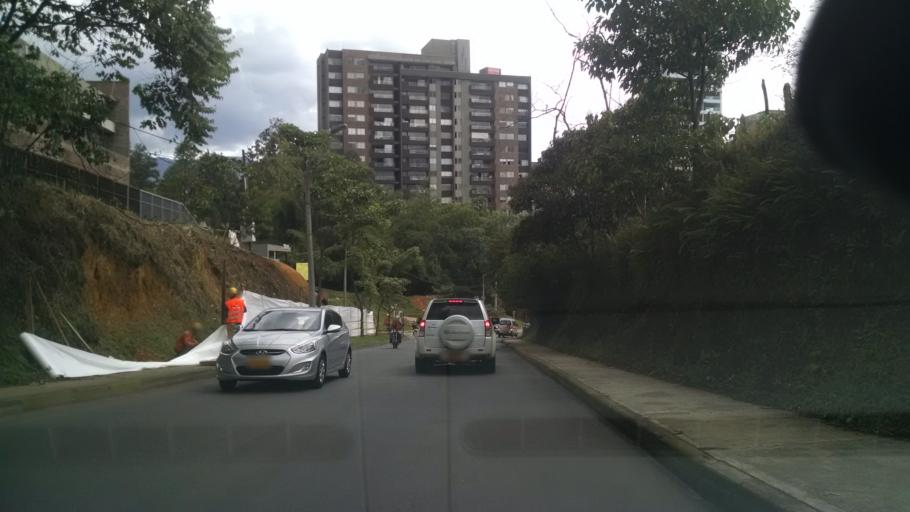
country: CO
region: Antioquia
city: Envigado
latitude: 6.1925
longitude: -75.5720
